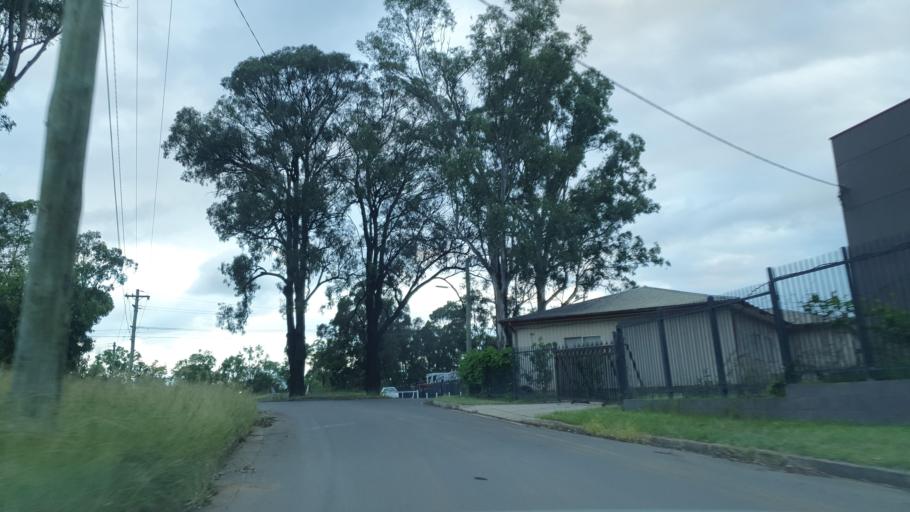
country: AU
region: New South Wales
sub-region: Penrith Municipality
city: Werrington County
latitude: -33.7450
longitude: 150.7713
